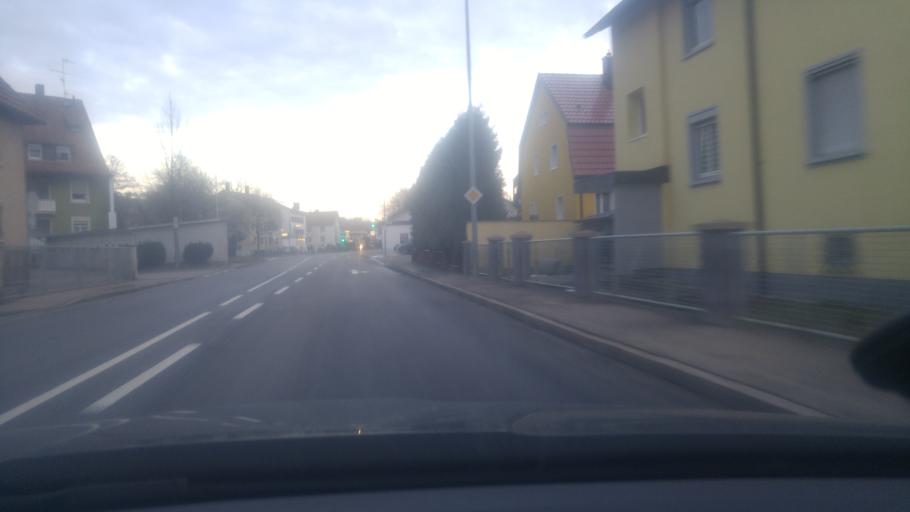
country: DE
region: Baden-Wuerttemberg
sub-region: Freiburg Region
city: Lauchringen
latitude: 47.6343
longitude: 8.2809
